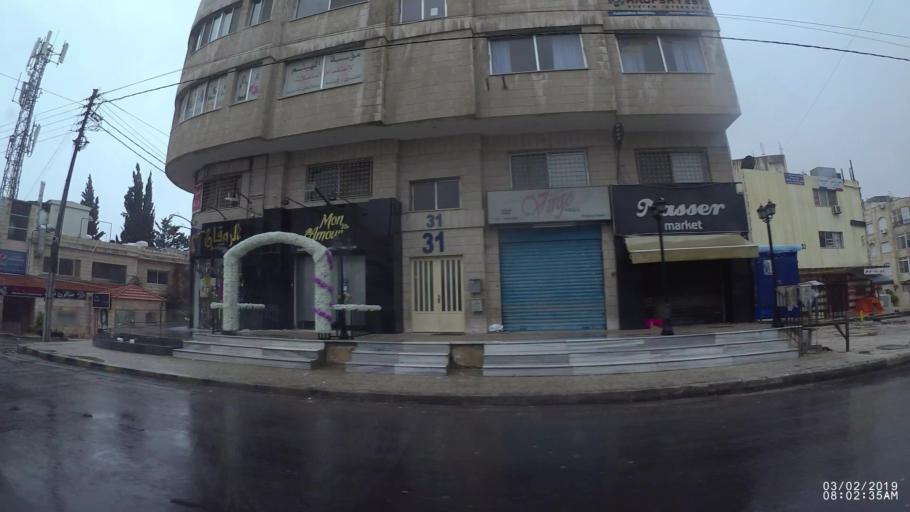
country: JO
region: Amman
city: Wadi as Sir
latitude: 31.9641
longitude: 35.8647
